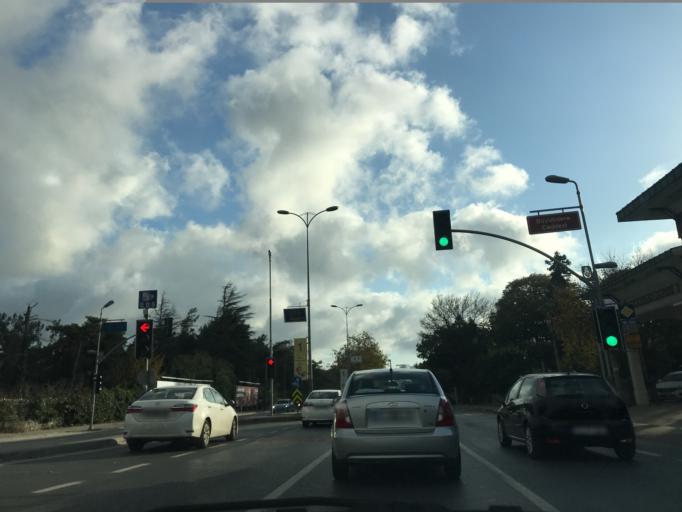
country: TR
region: Istanbul
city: Sisli
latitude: 41.1354
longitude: 29.0251
